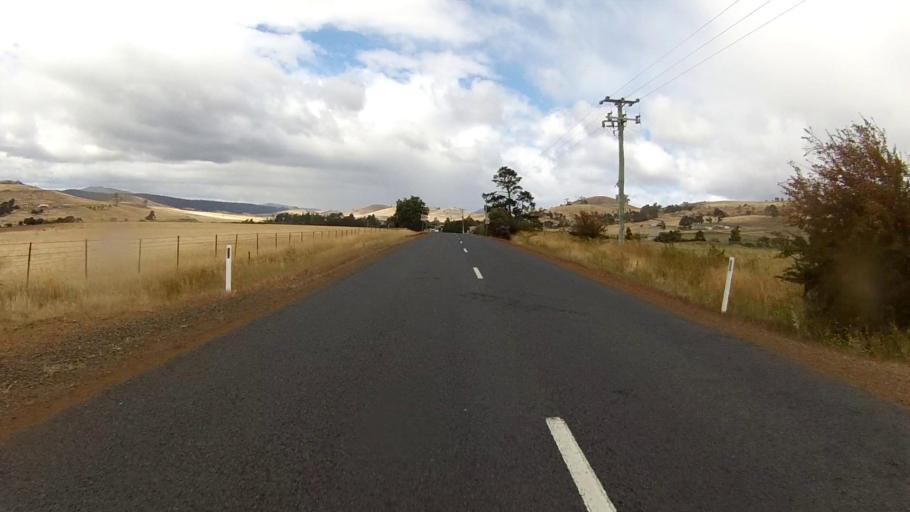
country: AU
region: Tasmania
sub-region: Brighton
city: Bridgewater
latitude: -42.5278
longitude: 147.3595
